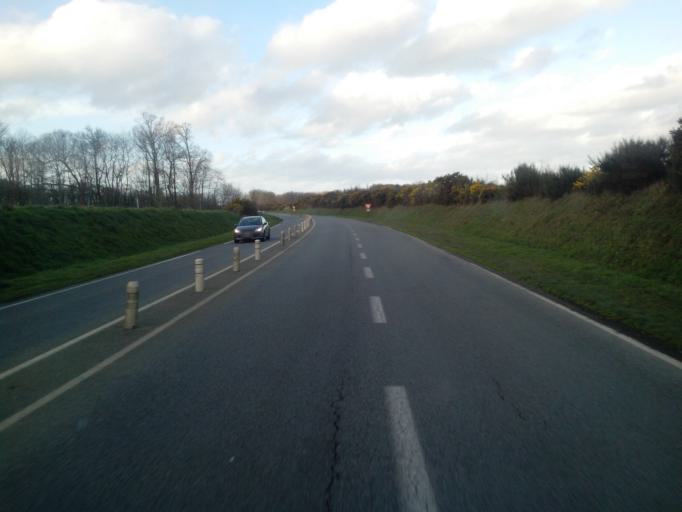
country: FR
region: Brittany
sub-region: Departement des Cotes-d'Armor
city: Pleslin-Trigavou
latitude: 48.5366
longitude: -2.0358
